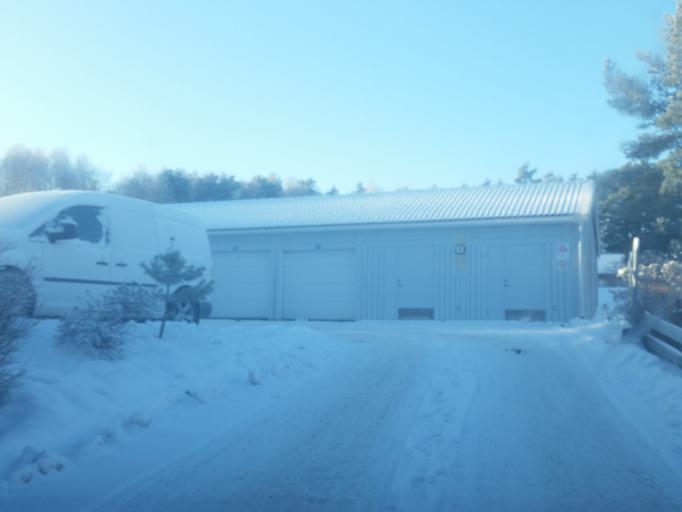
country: SE
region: Vaestra Goetaland
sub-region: Partille Kommun
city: Furulund
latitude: 57.7296
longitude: 12.1313
